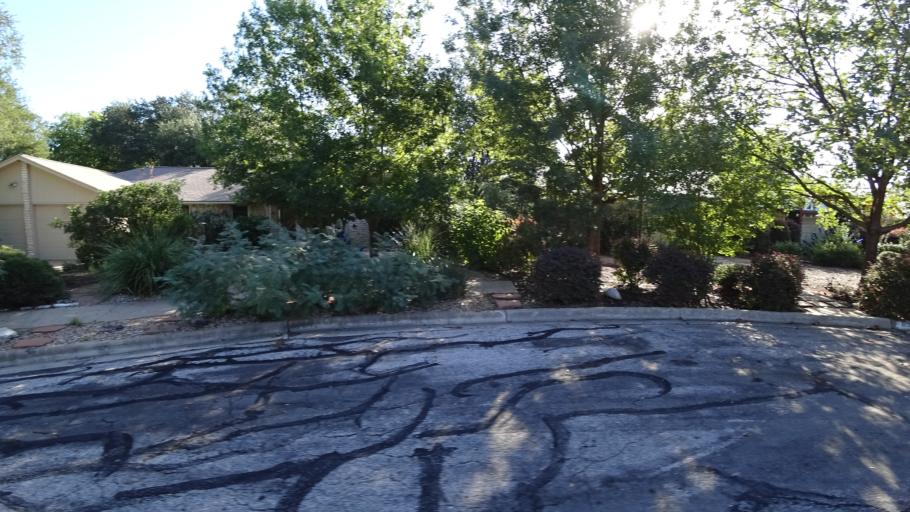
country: US
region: Texas
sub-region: Travis County
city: Rollingwood
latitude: 30.2100
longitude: -97.8093
